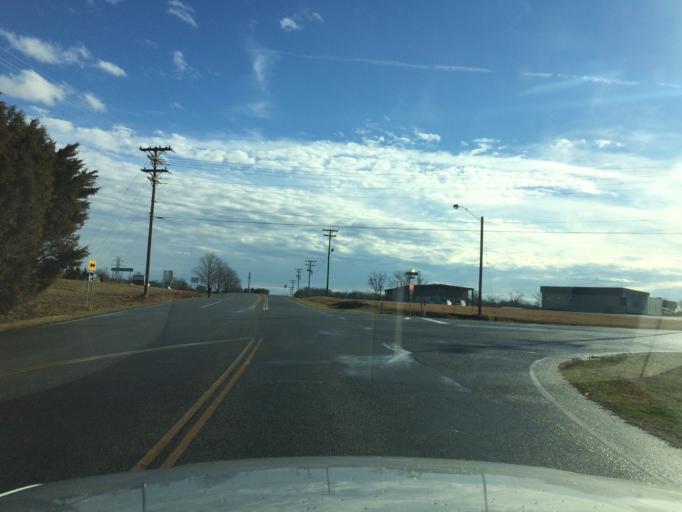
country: US
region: South Carolina
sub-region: Spartanburg County
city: Fairforest
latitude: 34.9631
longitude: -82.0355
